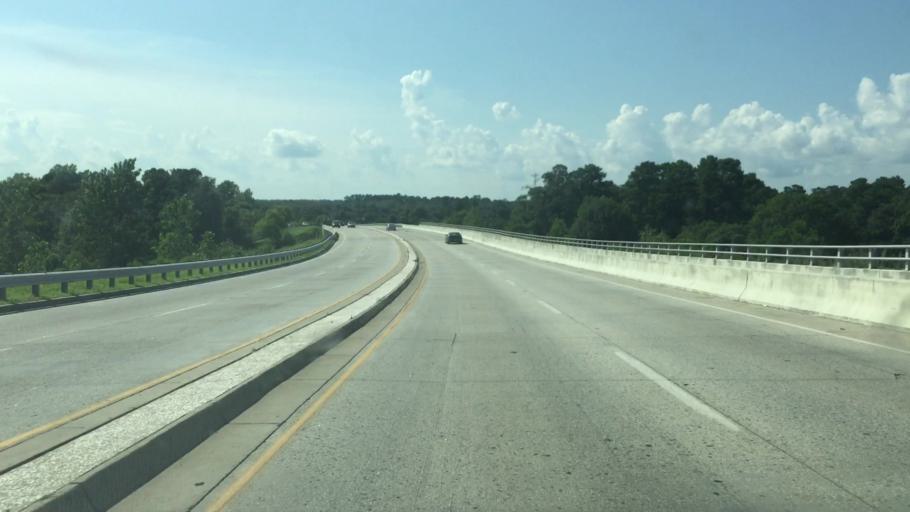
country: US
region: South Carolina
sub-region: Horry County
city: North Myrtle Beach
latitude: 33.8352
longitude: -78.6855
